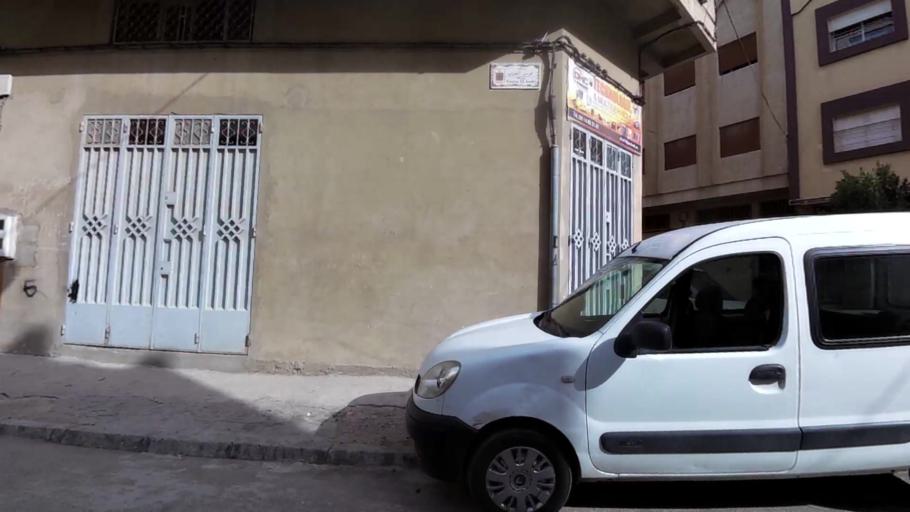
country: MA
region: Tanger-Tetouan
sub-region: Tanger-Assilah
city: Tangier
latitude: 35.7533
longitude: -5.7946
